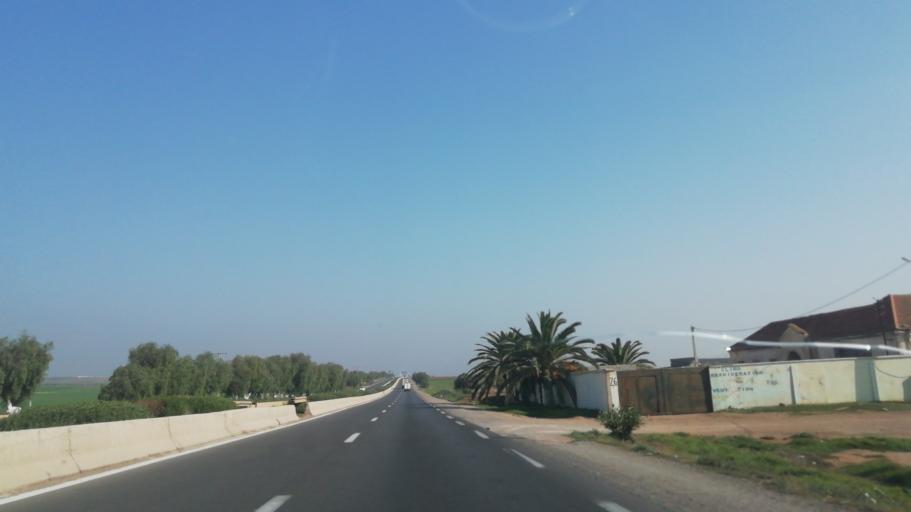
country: DZ
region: Ain Temouchent
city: El Amria
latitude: 35.5404
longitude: -0.9763
